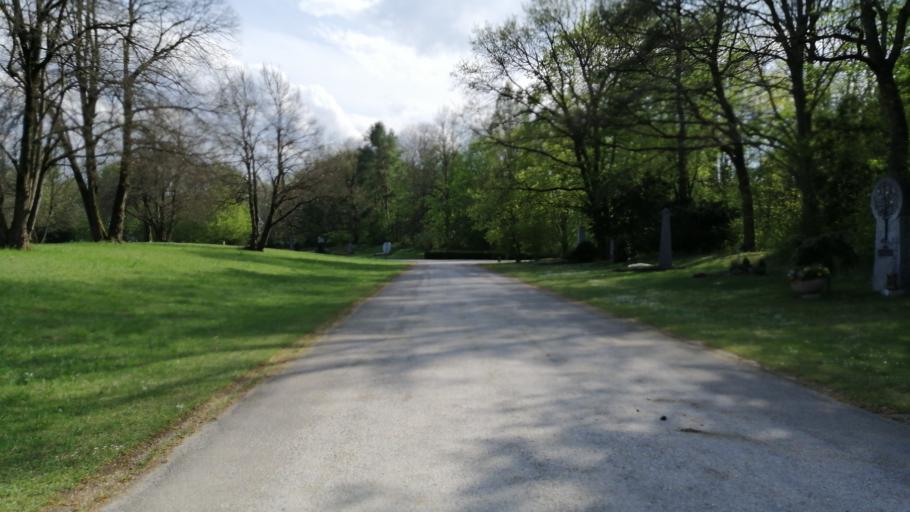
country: DE
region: Bavaria
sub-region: Upper Bavaria
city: Unterhaching
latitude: 48.0986
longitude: 11.6195
